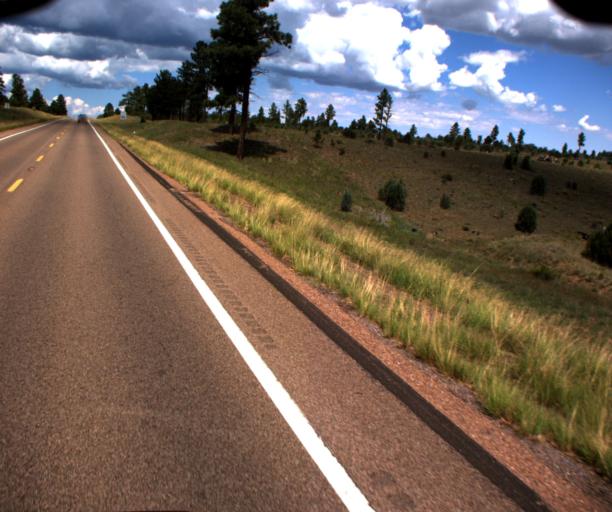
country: US
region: Arizona
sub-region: Navajo County
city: Heber-Overgaard
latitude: 34.3854
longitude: -110.4965
